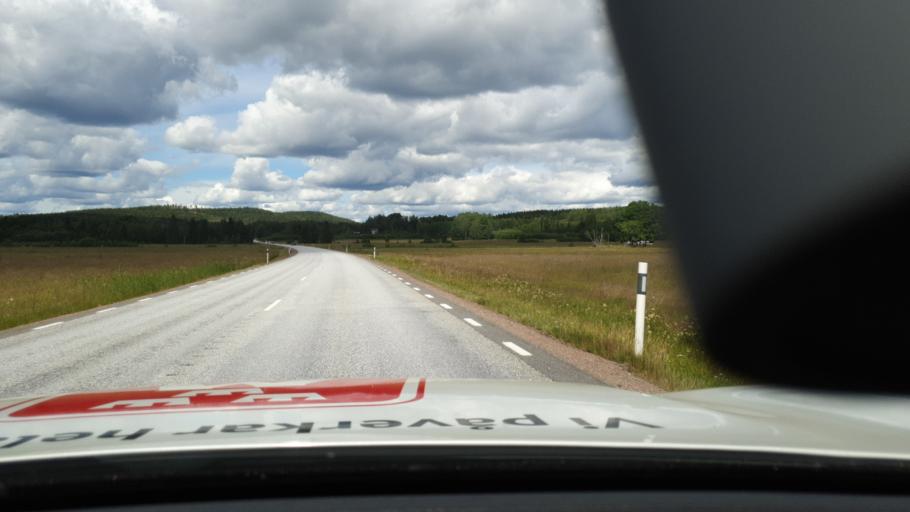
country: SE
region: Vaermland
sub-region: Storfors Kommun
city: Storfors
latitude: 59.4978
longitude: 14.3235
